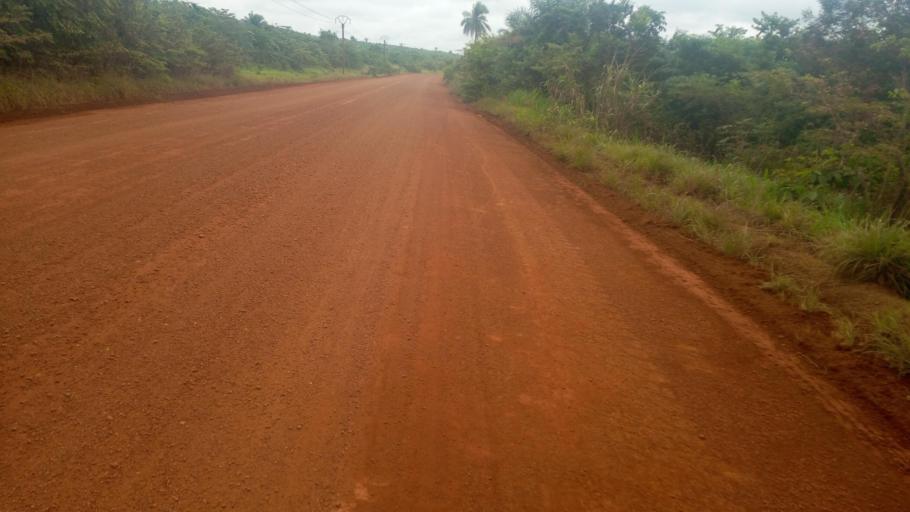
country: SL
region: Southern Province
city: Mogbwemo
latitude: 7.7181
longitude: -12.2855
